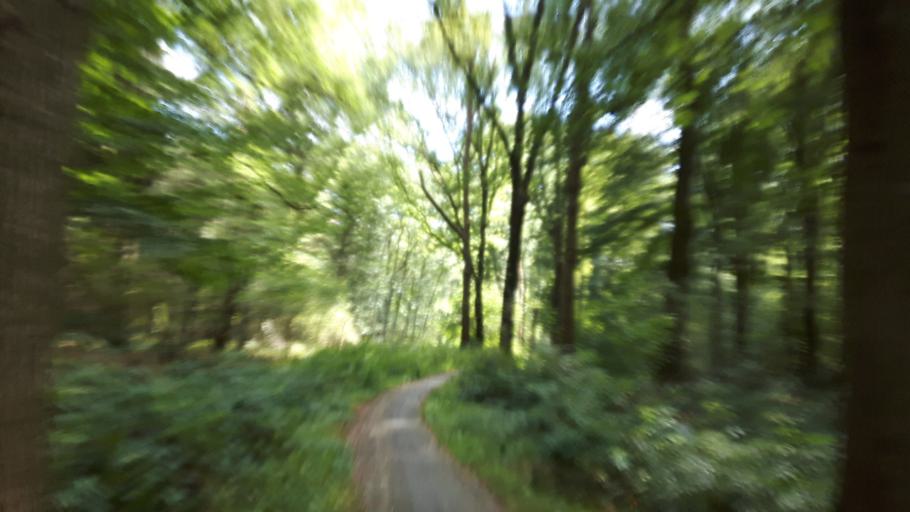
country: NL
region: Friesland
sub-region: Gemeente Smallingerland
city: Drachtstercompagnie
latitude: 53.0692
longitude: 6.2059
